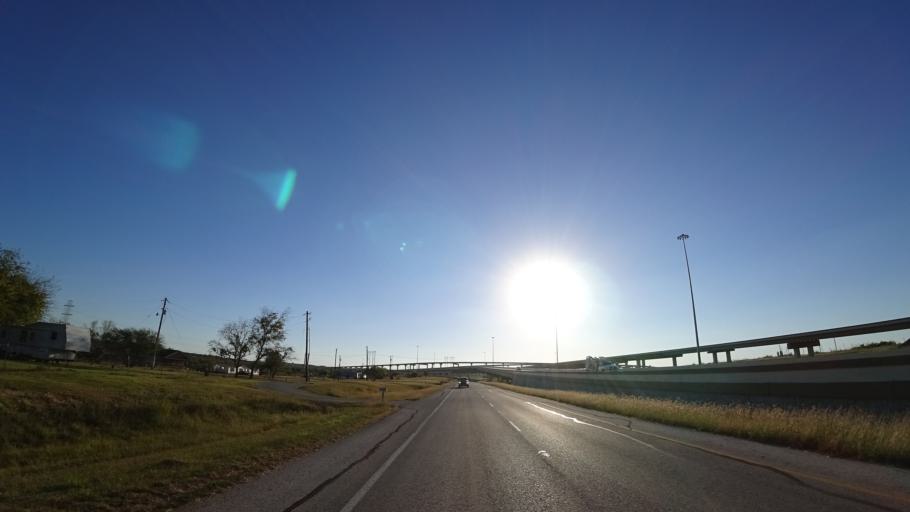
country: US
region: Texas
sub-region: Travis County
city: Onion Creek
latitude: 30.0841
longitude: -97.6866
